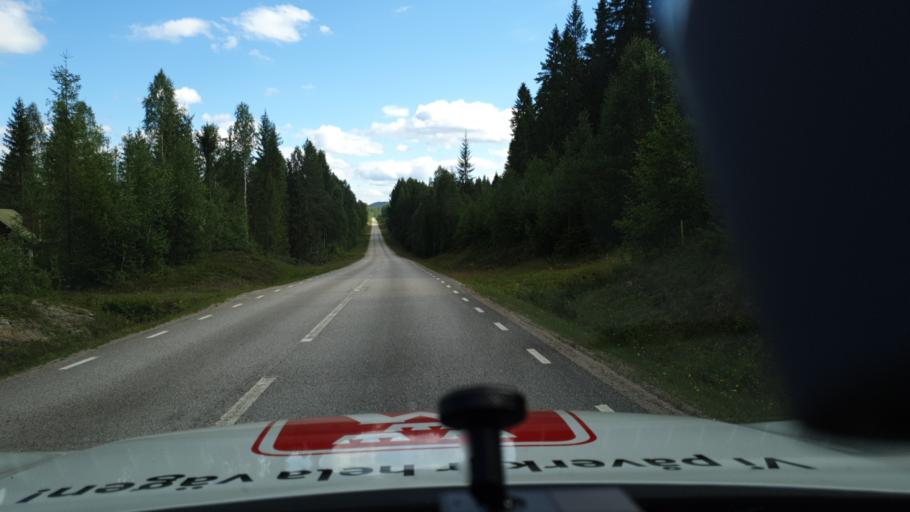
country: NO
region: Hedmark
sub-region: Trysil
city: Innbygda
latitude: 61.0220
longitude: 12.4686
